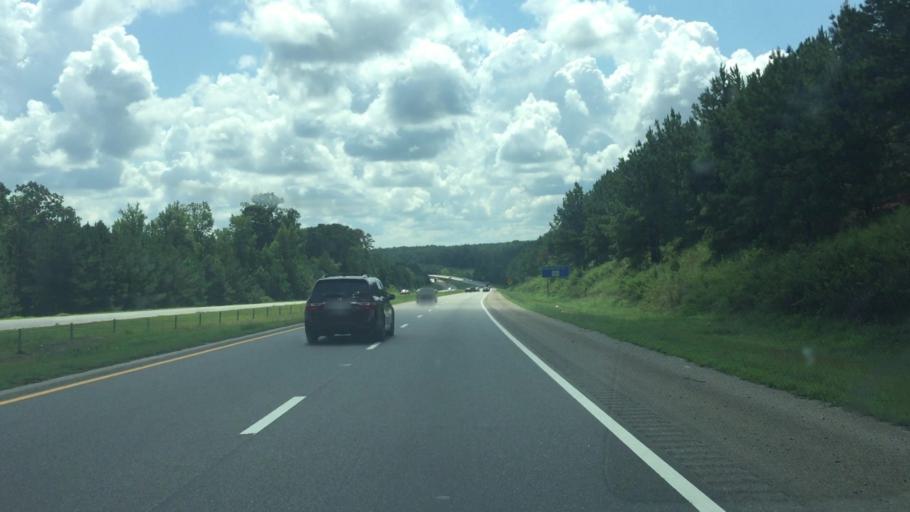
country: US
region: North Carolina
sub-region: Richmond County
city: Cordova
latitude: 34.9271
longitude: -79.8214
